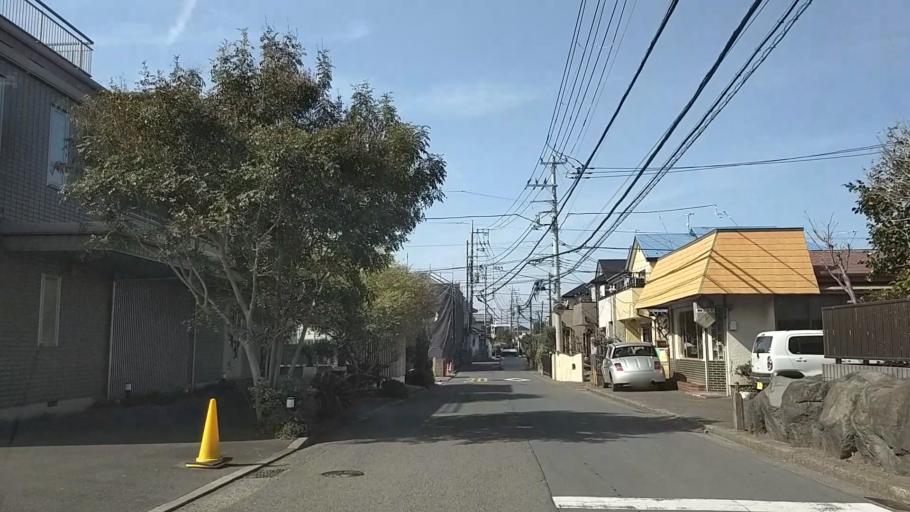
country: JP
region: Kanagawa
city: Chigasaki
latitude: 35.3466
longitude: 139.4236
